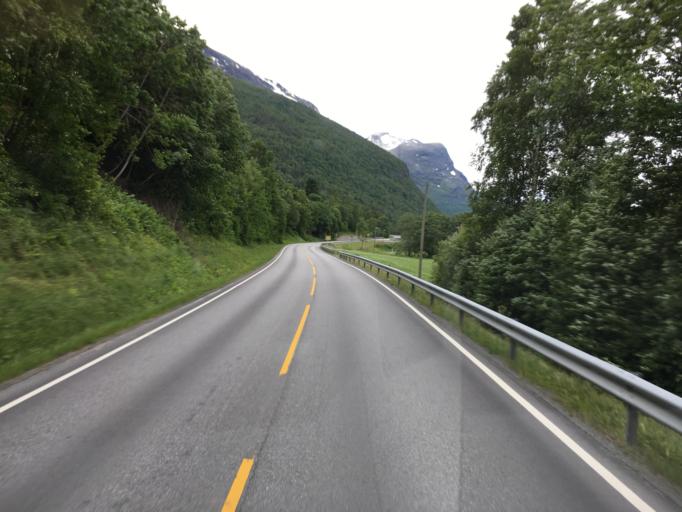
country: NO
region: More og Romsdal
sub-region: Sunndal
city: Sunndalsora
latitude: 62.6438
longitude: 8.7316
